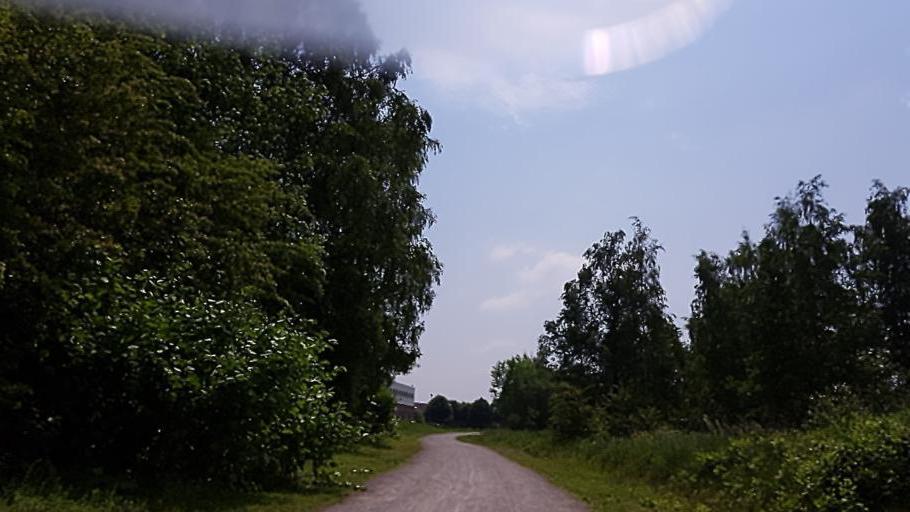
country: FR
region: Nord-Pas-de-Calais
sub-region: Departement du Nord
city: Vieux-Conde
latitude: 50.4608
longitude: 3.5745
